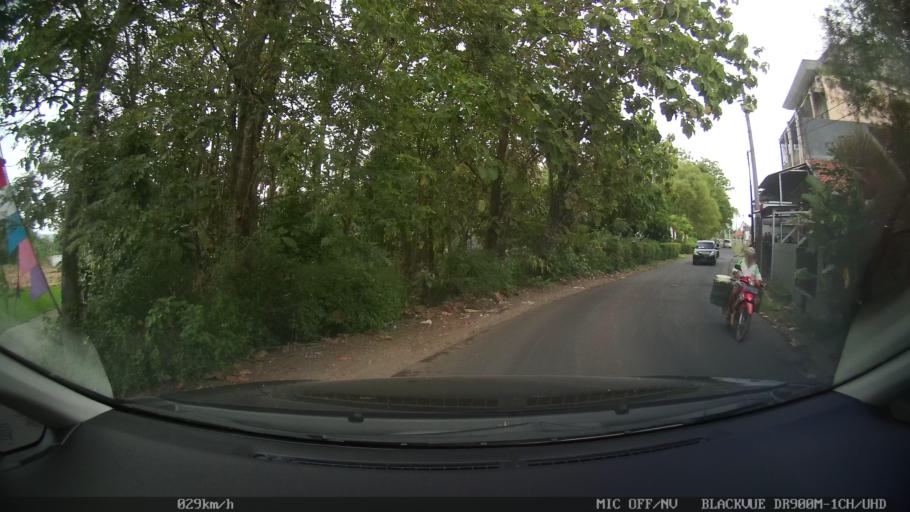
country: ID
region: Daerah Istimewa Yogyakarta
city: Sewon
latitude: -7.8590
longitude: 110.4219
